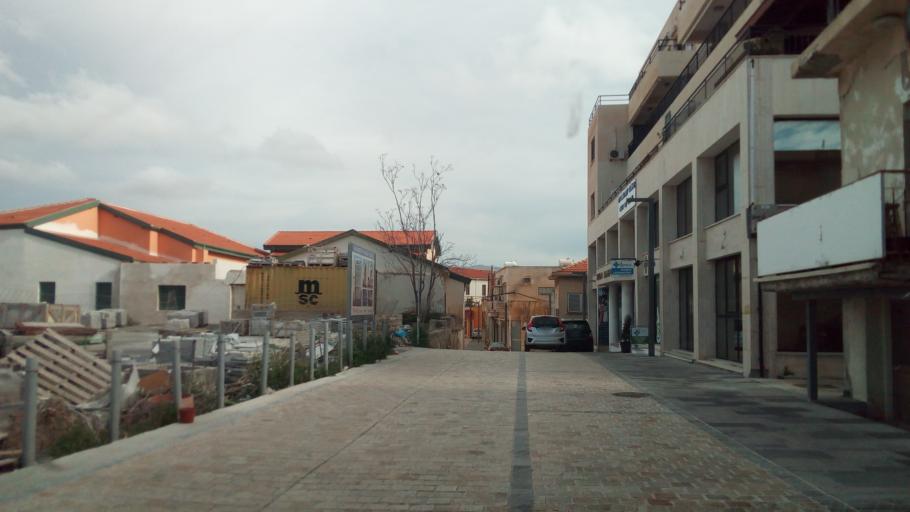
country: CY
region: Pafos
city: Paphos
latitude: 34.7759
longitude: 32.4194
